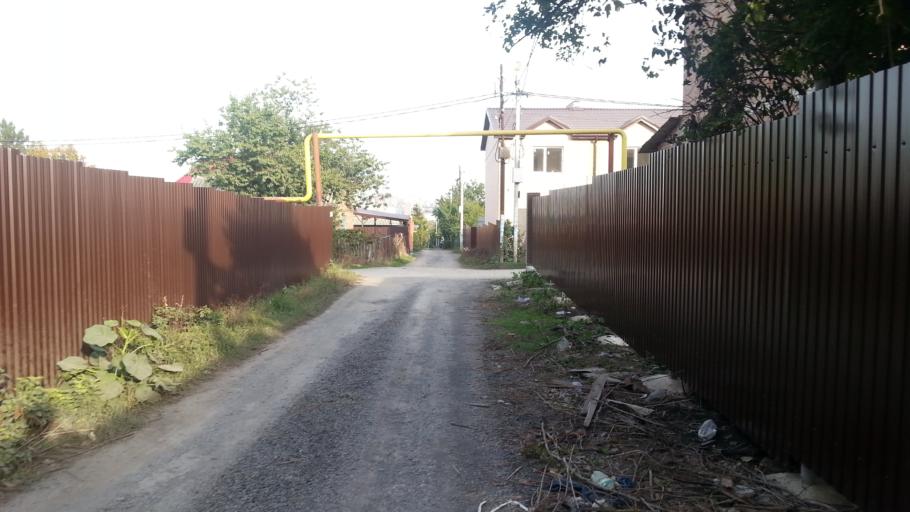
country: RU
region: Rostov
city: Severnyy
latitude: 47.2883
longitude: 39.6698
